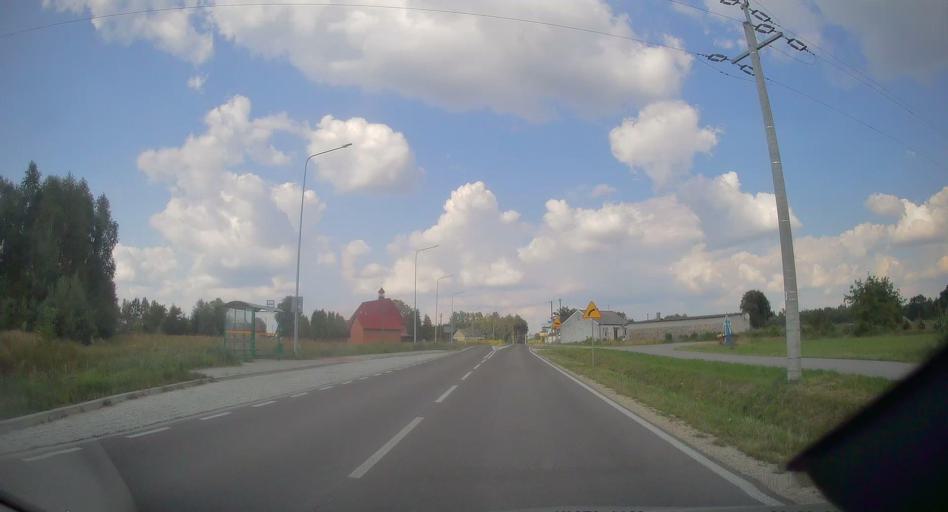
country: PL
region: Swietokrzyskie
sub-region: Powiat kielecki
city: Lopuszno
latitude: 50.9857
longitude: 20.2555
